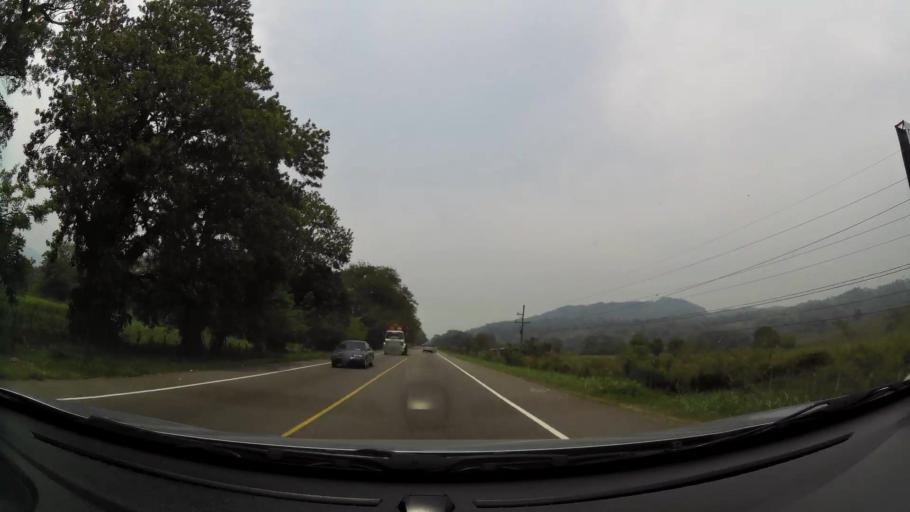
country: HN
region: Cortes
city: La Guama
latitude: 14.8200
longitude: -87.9620
